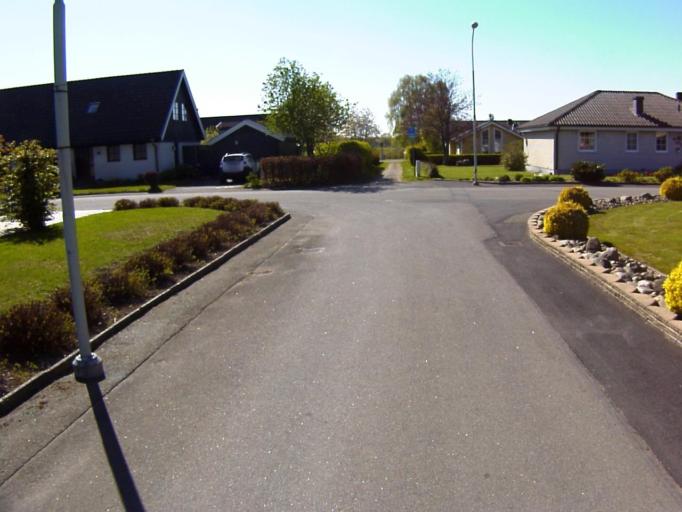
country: SE
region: Skane
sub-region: Kristianstads Kommun
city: Kristianstad
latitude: 56.0335
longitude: 14.1958
